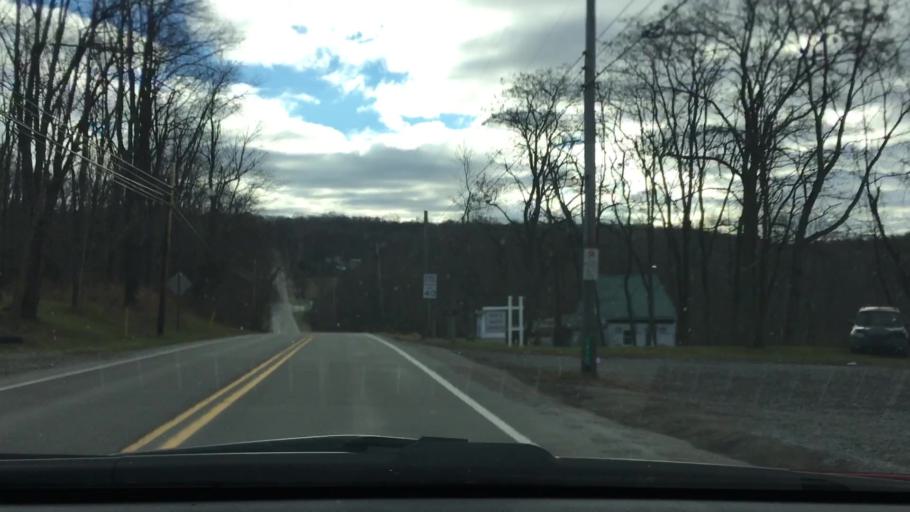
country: US
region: Pennsylvania
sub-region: Armstrong County
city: Orchard Hills
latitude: 40.6070
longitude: -79.4713
